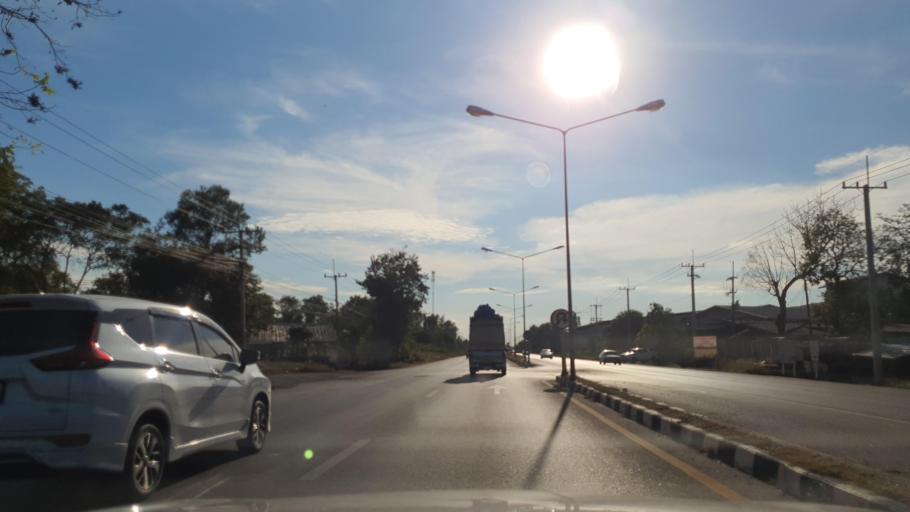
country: TH
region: Maha Sarakham
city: Kantharawichai
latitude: 16.3592
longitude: 103.3367
